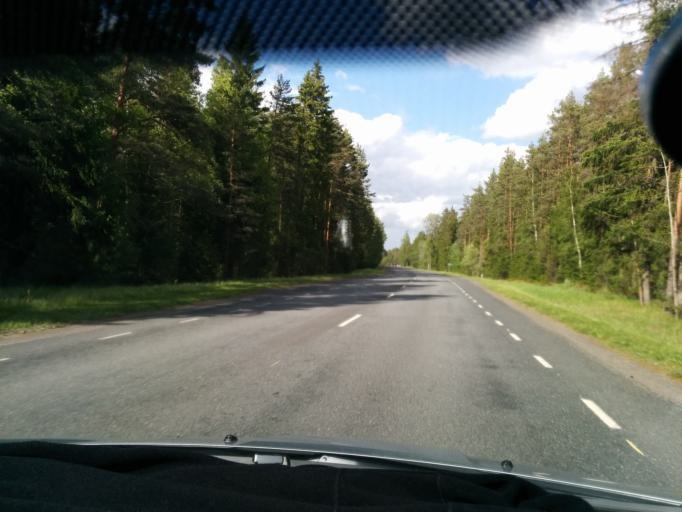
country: EE
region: Harju
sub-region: Loksa linn
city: Loksa
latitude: 59.5369
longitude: 25.7307
